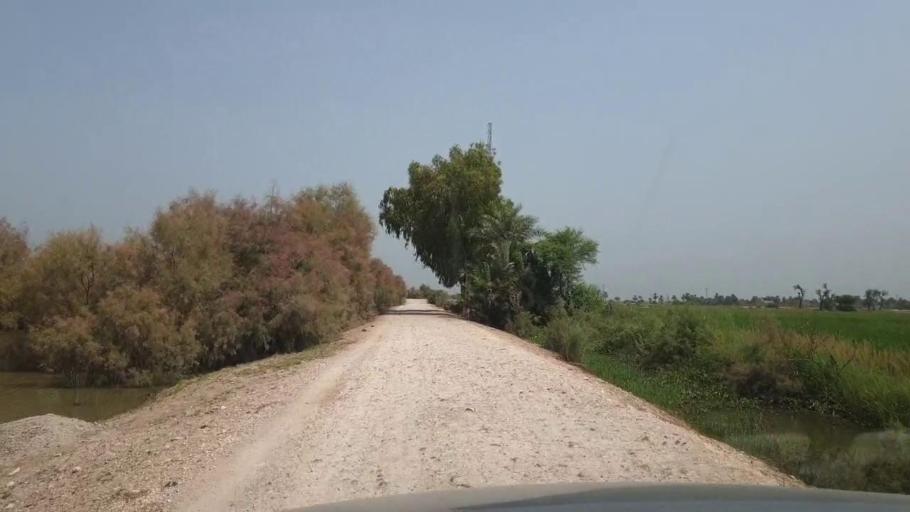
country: PK
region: Sindh
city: Madeji
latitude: 27.8024
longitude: 68.5318
